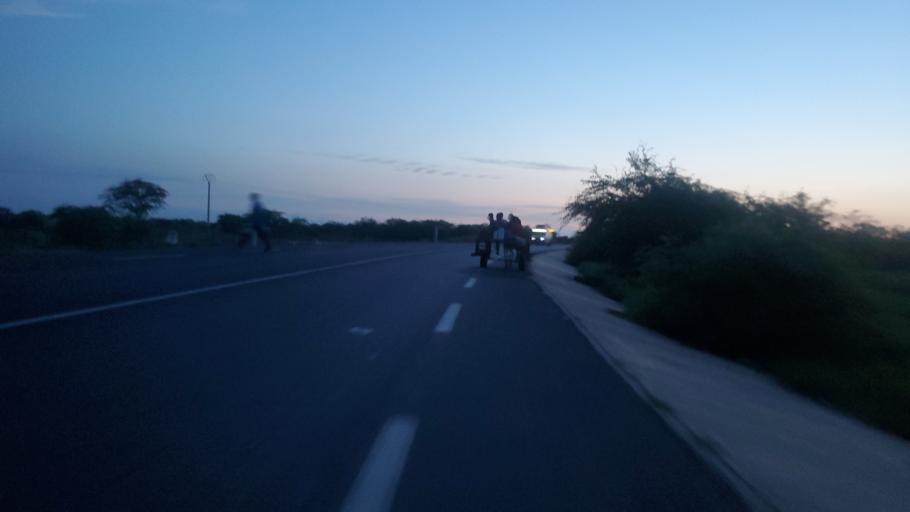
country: SN
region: Saint-Louis
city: Saint-Louis
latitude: 16.0571
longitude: -16.3989
